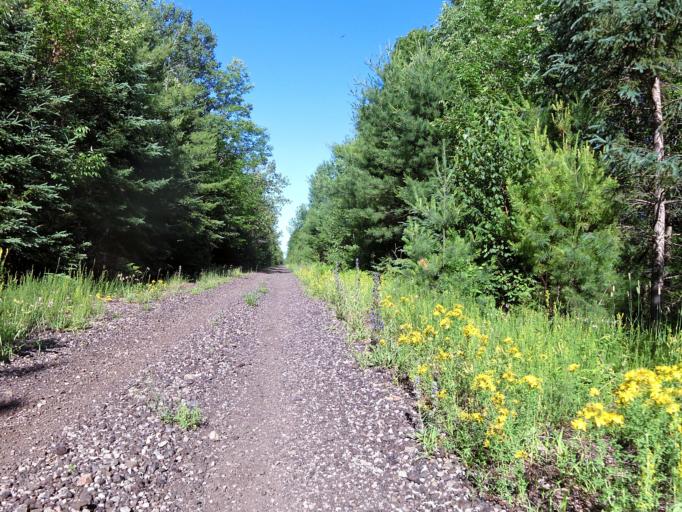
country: CA
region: Ontario
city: Arnprior
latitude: 45.4590
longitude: -76.2448
